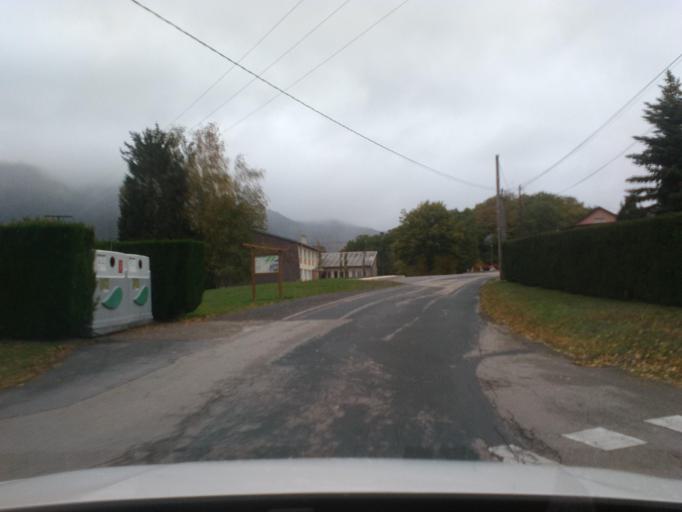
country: FR
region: Lorraine
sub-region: Departement des Vosges
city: Sainte-Marguerite
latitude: 48.2841
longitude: 6.9977
